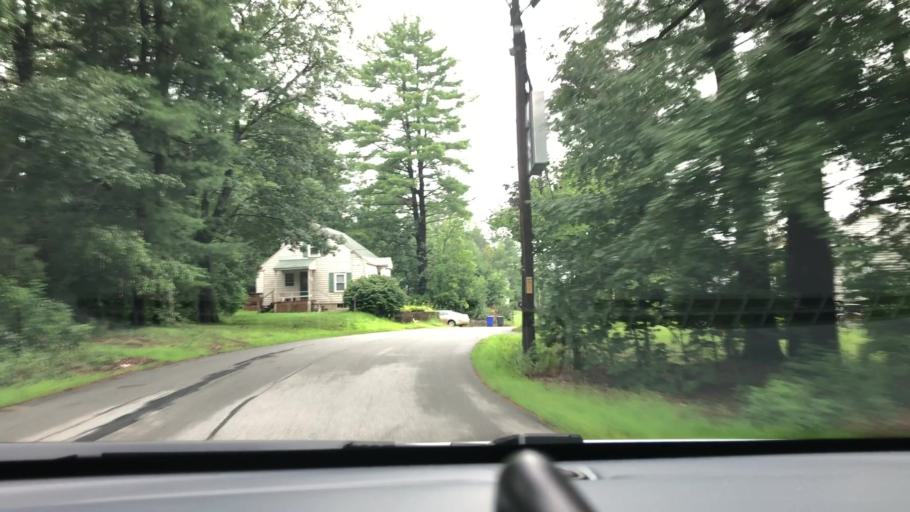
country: US
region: New Hampshire
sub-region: Hillsborough County
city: Pinardville
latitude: 43.0057
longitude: -71.5214
